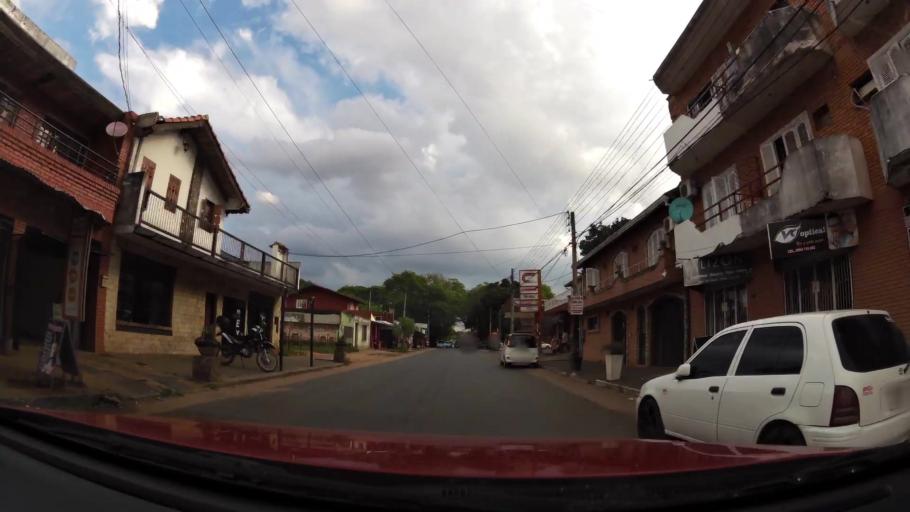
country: PY
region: Central
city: Fernando de la Mora
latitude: -25.3406
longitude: -57.5456
